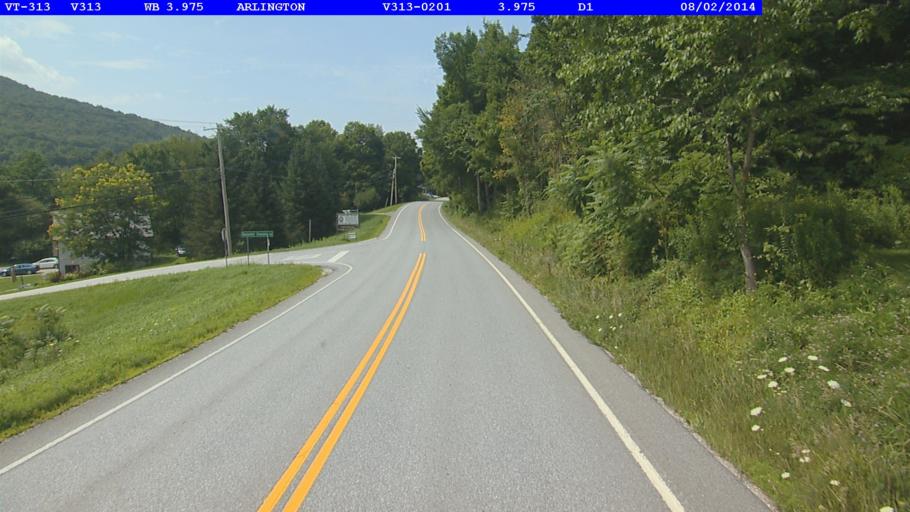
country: US
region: Vermont
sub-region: Bennington County
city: Arlington
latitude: 43.0917
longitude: -73.1973
